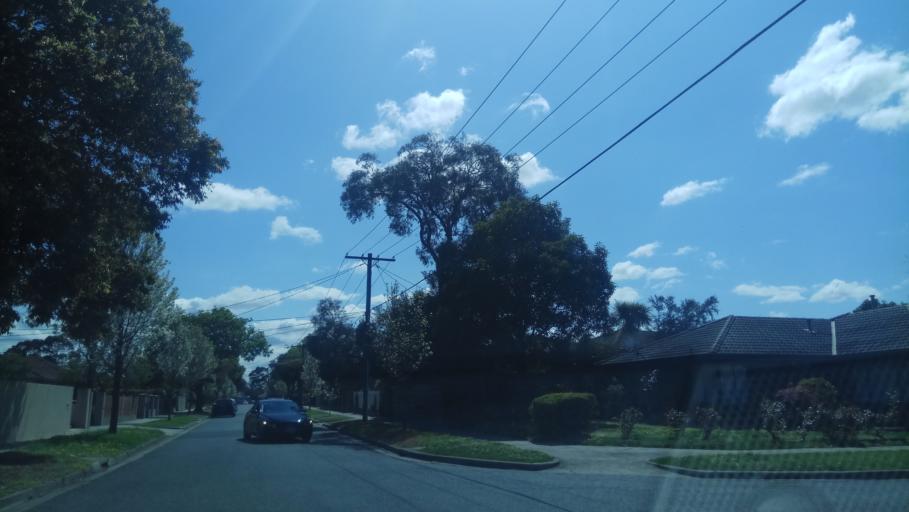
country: AU
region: Victoria
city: Heatherton
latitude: -37.9659
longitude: 145.0813
